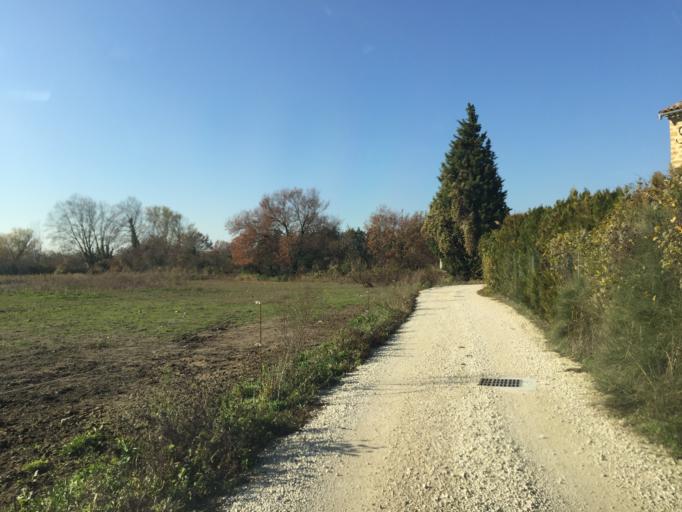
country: FR
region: Provence-Alpes-Cote d'Azur
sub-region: Departement du Vaucluse
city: Entraigues-sur-la-Sorgue
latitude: 44.0132
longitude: 4.9290
